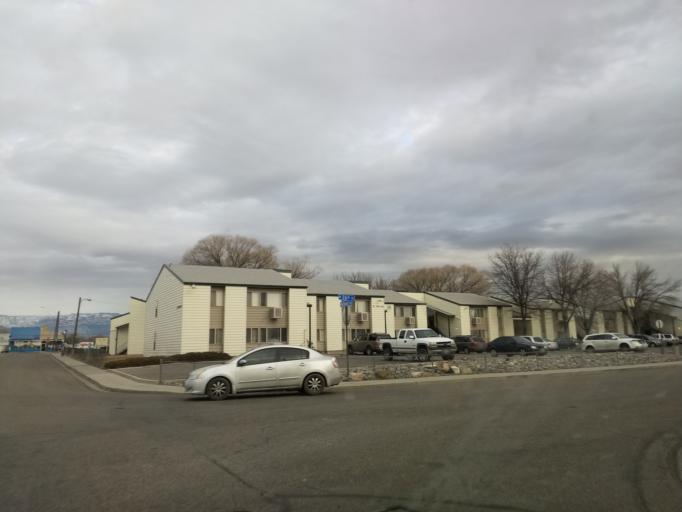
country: US
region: Colorado
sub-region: Mesa County
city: Grand Junction
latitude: 39.0755
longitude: -108.5354
